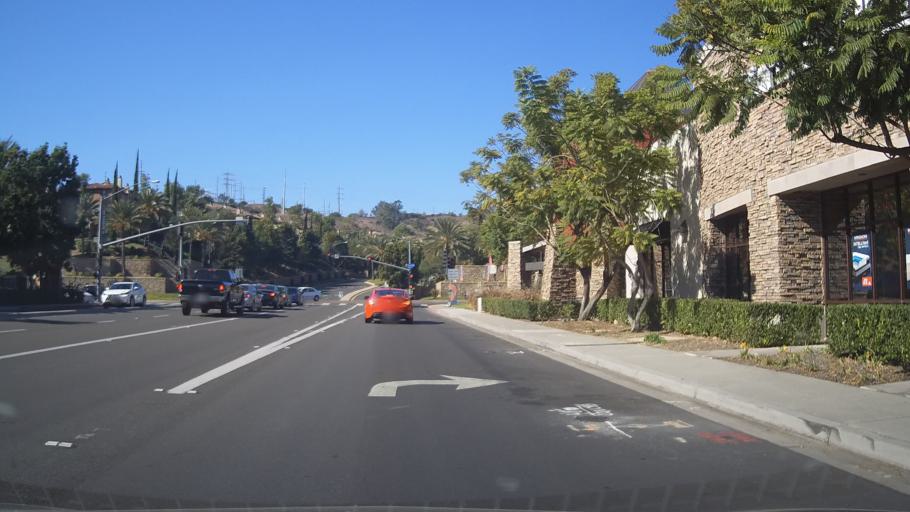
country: US
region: California
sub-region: San Diego County
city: San Diego
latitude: 32.7807
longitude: -117.1307
